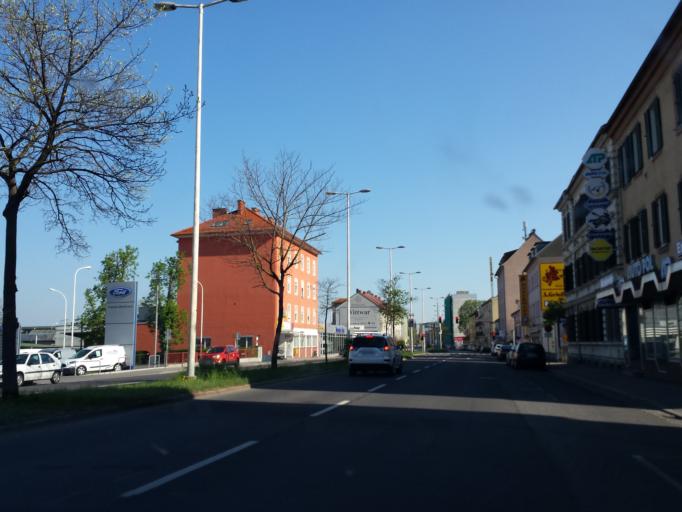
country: AT
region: Styria
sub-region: Graz Stadt
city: Goesting
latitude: 47.0925
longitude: 15.4068
